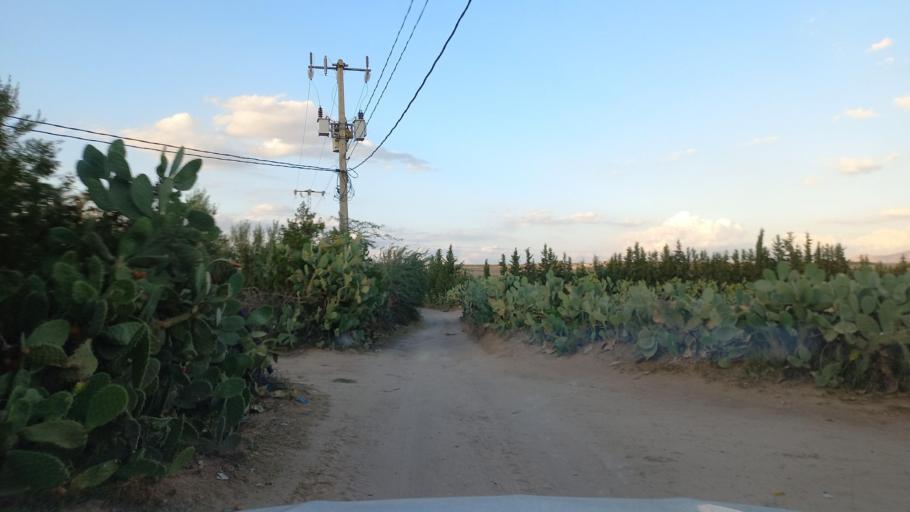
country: TN
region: Al Qasrayn
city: Sbiba
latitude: 35.3783
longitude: 9.0560
